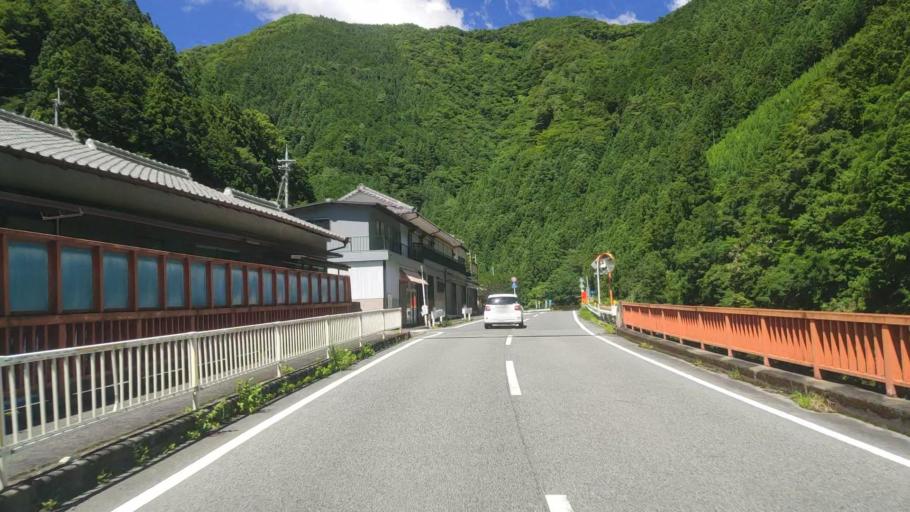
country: JP
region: Mie
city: Owase
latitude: 34.1803
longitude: 136.0053
